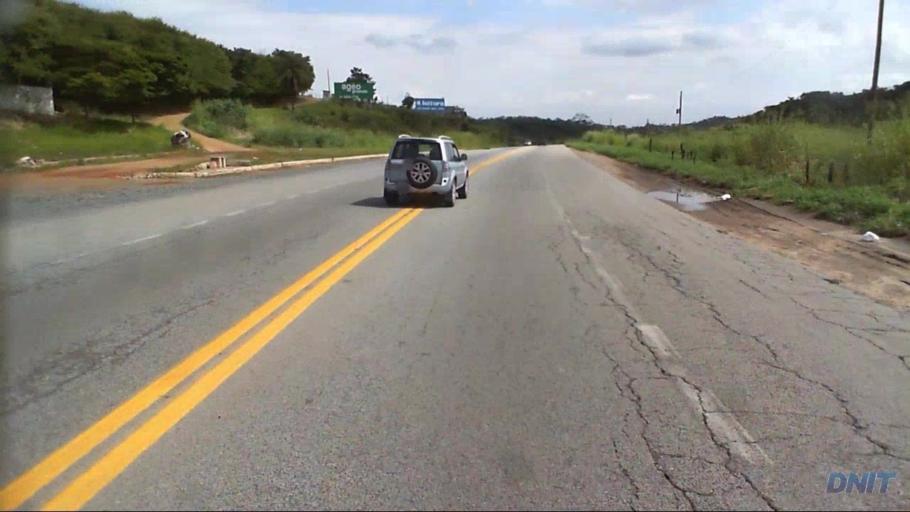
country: BR
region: Minas Gerais
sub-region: Santa Luzia
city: Santa Luzia
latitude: -19.8132
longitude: -43.7983
